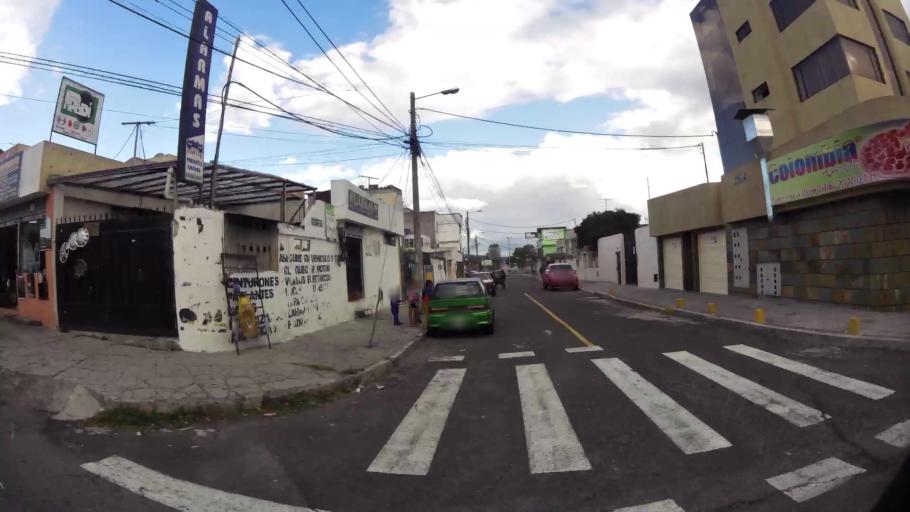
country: EC
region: Pichincha
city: Quito
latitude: -0.1379
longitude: -78.4789
